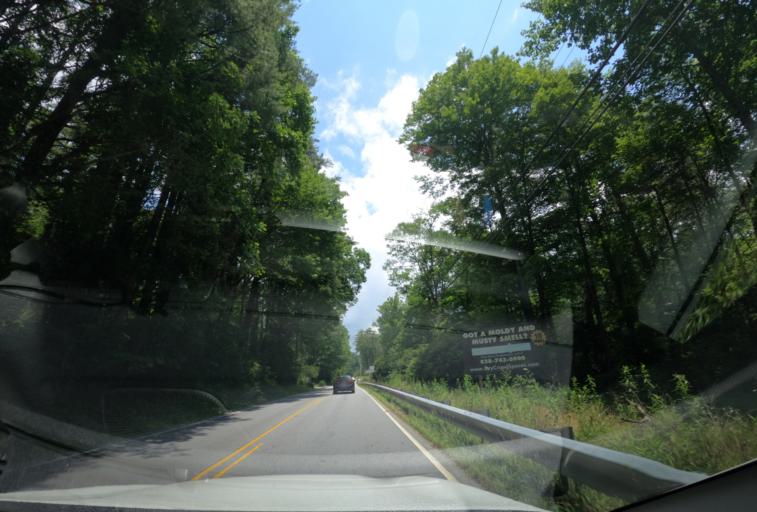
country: US
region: North Carolina
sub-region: Jackson County
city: Cullowhee
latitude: 35.1096
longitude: -83.1173
